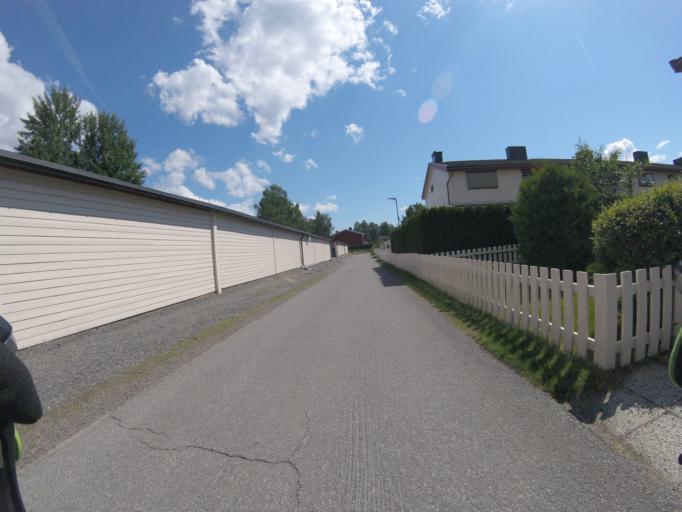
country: NO
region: Akershus
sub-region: Skedsmo
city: Lillestrom
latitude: 59.9529
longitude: 11.0541
